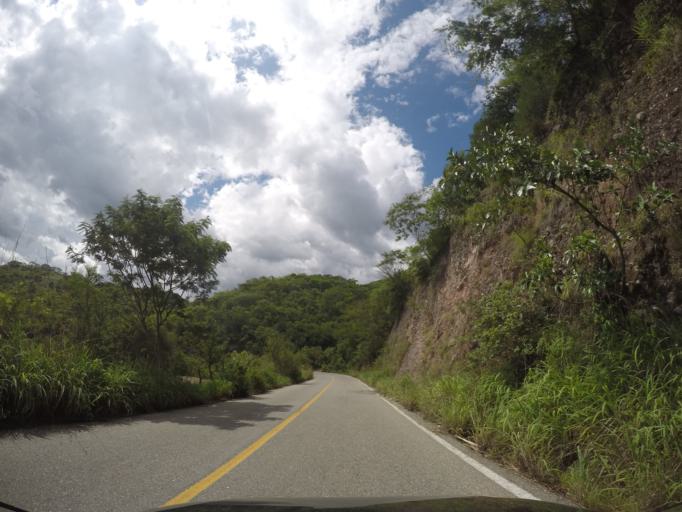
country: MX
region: Oaxaca
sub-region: San Jeronimo Coatlan
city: San Cristobal Honduras
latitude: 16.4351
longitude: -97.0548
